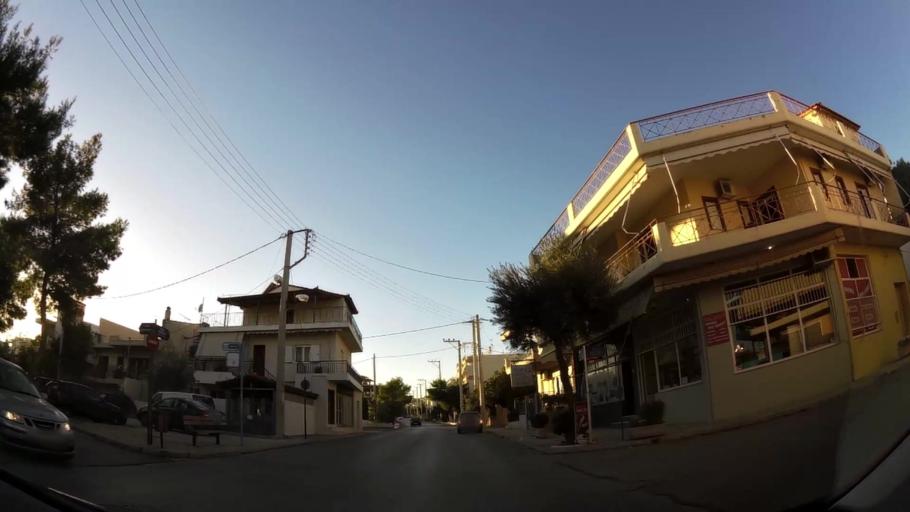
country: GR
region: Attica
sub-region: Nomarchia Dytikis Attikis
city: Ano Liosia
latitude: 38.0876
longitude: 23.7048
